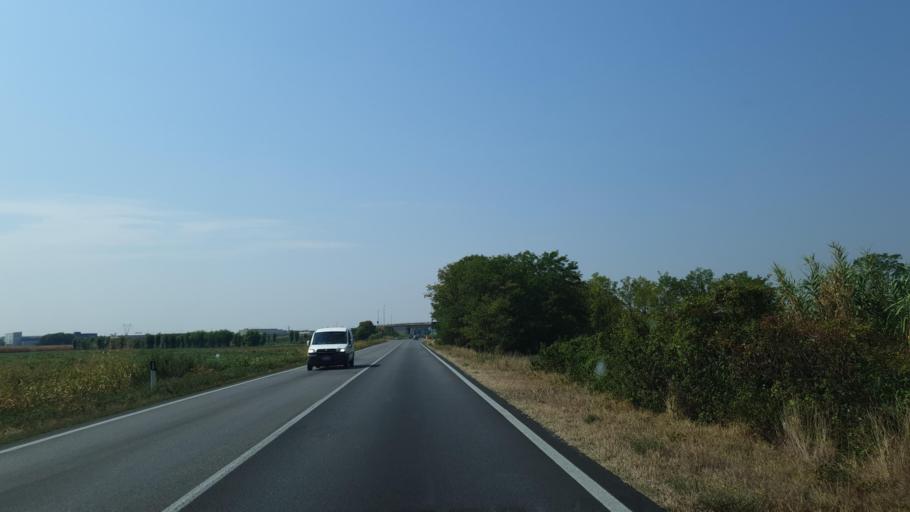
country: IT
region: Lombardy
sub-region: Provincia di Brescia
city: Leno
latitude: 45.3817
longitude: 10.2317
